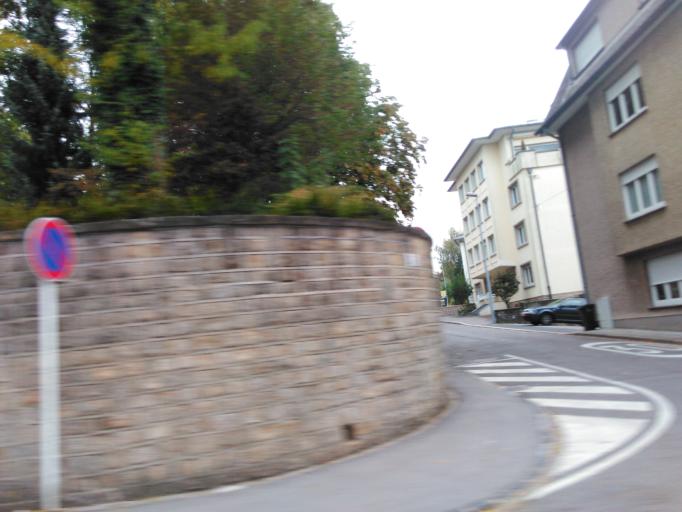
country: LU
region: Luxembourg
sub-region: Canton de Luxembourg
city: Luxembourg
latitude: 49.6220
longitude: 6.1121
